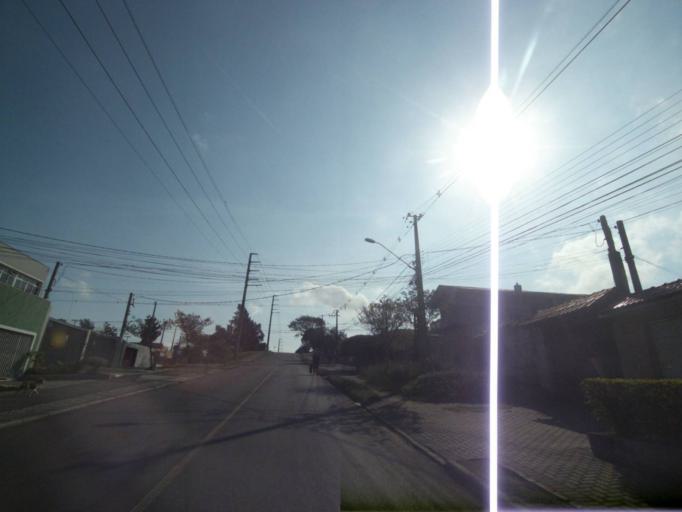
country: BR
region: Parana
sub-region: Pinhais
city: Pinhais
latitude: -25.4033
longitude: -49.1985
